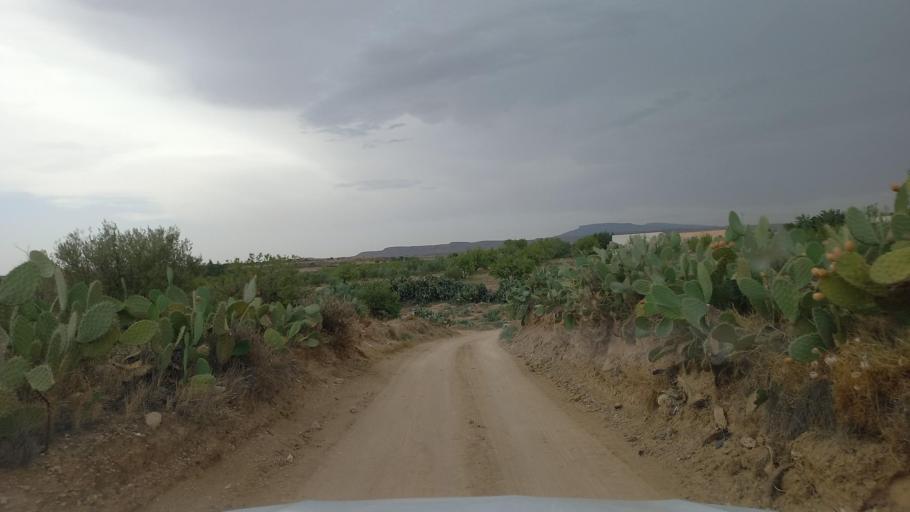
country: TN
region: Al Qasrayn
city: Kasserine
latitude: 35.2390
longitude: 9.0245
